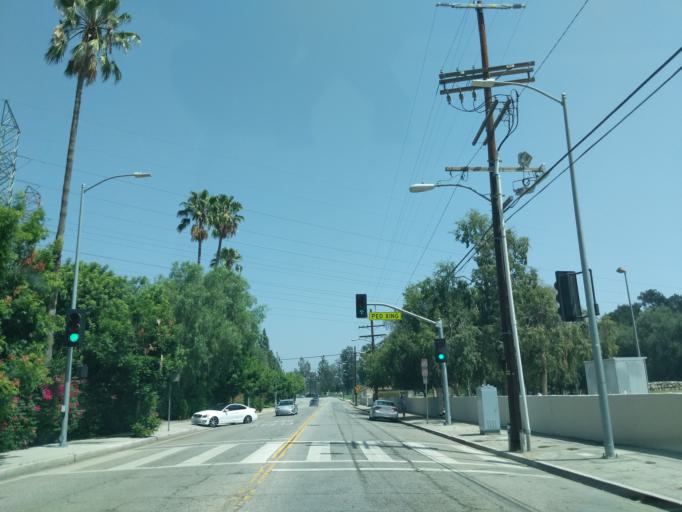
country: US
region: California
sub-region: Los Angeles County
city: San Fernando
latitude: 34.2727
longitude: -118.4613
